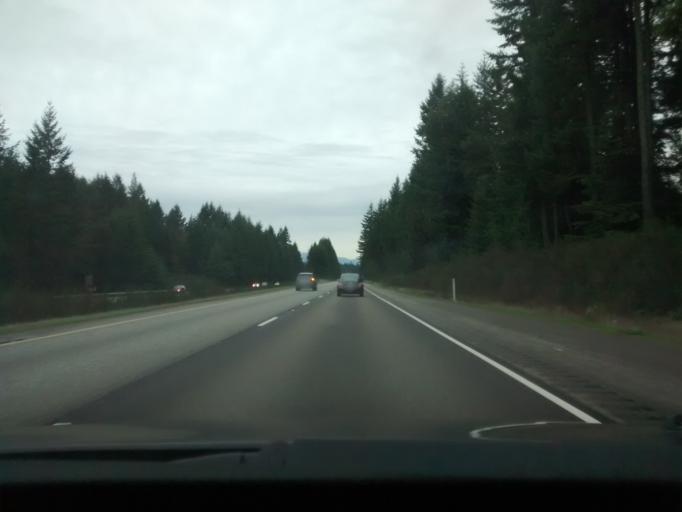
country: US
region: Washington
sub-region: Kitsap County
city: Bethel
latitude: 47.4919
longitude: -122.6363
